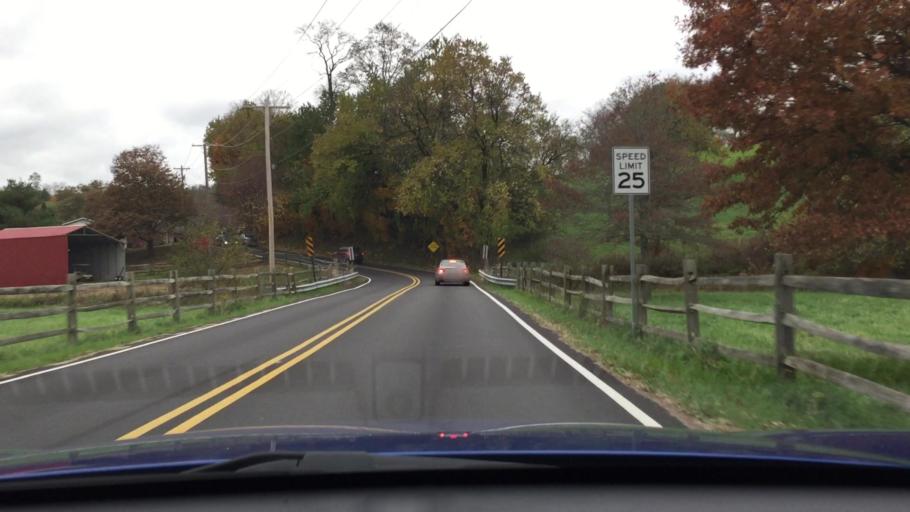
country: US
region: Pennsylvania
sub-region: Washington County
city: East Washington
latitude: 40.1986
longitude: -80.2227
